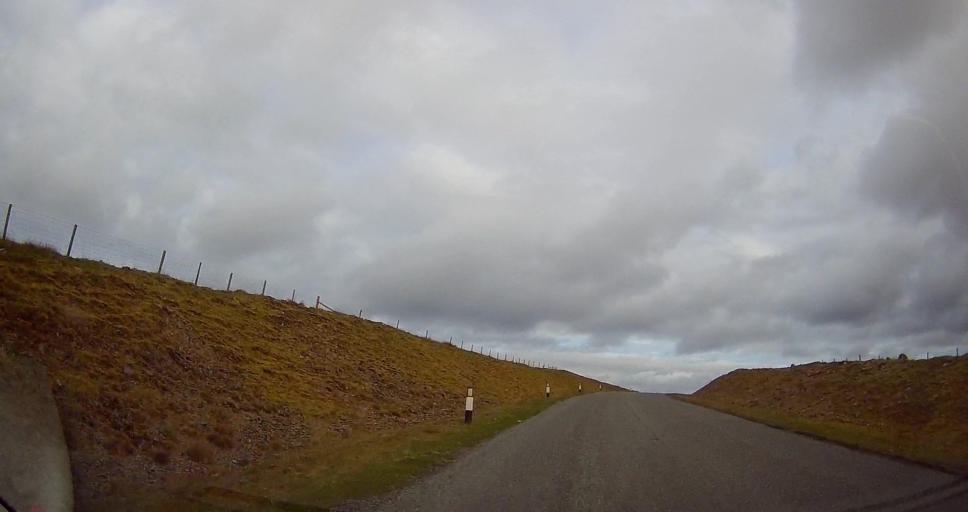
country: GB
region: Scotland
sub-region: Shetland Islands
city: Shetland
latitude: 60.5014
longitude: -1.1608
